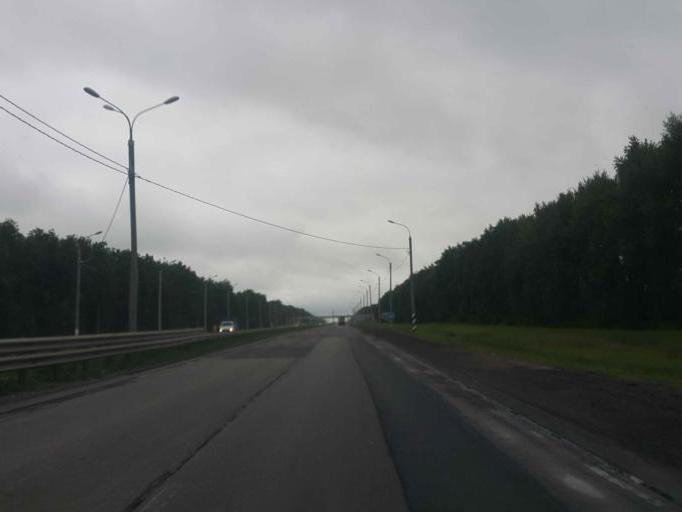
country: RU
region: Tambov
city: Selezni
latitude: 52.7581
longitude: 41.1459
